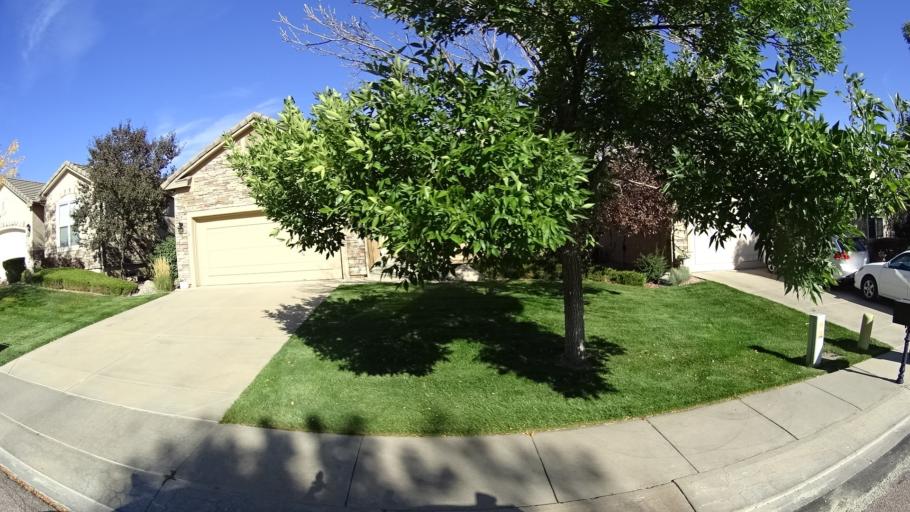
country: US
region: Colorado
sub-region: El Paso County
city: Colorado Springs
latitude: 38.9021
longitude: -104.7918
